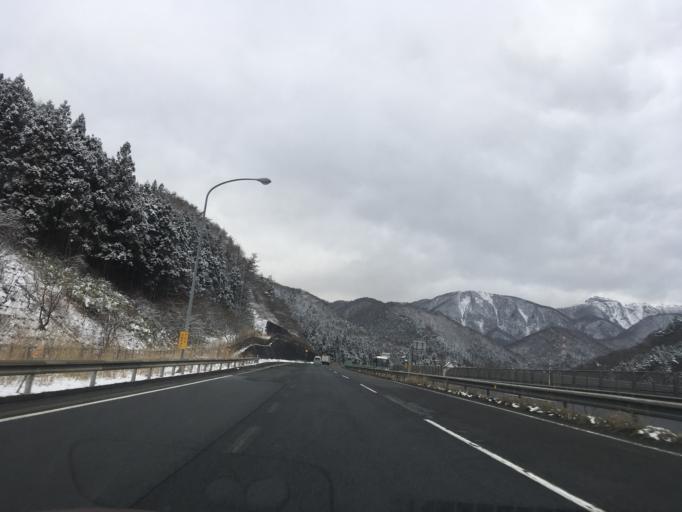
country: JP
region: Yamagata
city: Yamagata-shi
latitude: 38.2237
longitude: 140.5079
